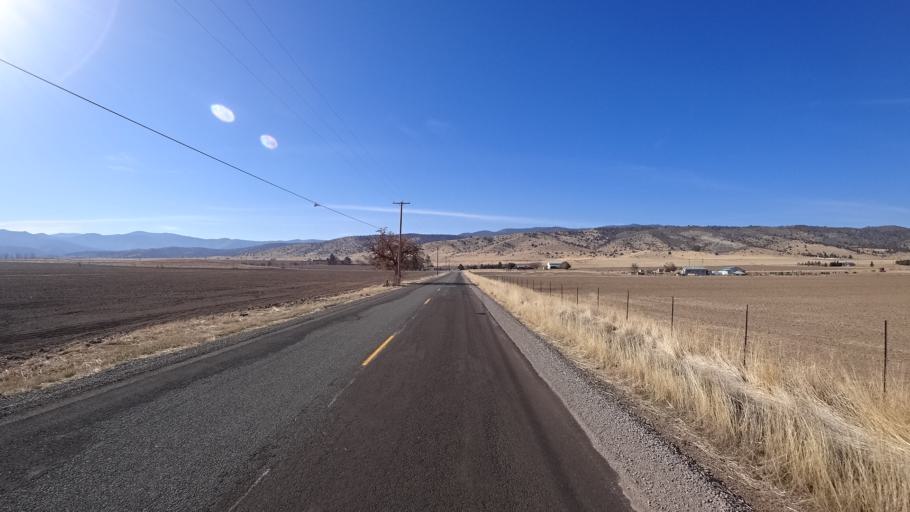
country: US
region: California
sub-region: Siskiyou County
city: Montague
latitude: 41.5747
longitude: -122.5437
